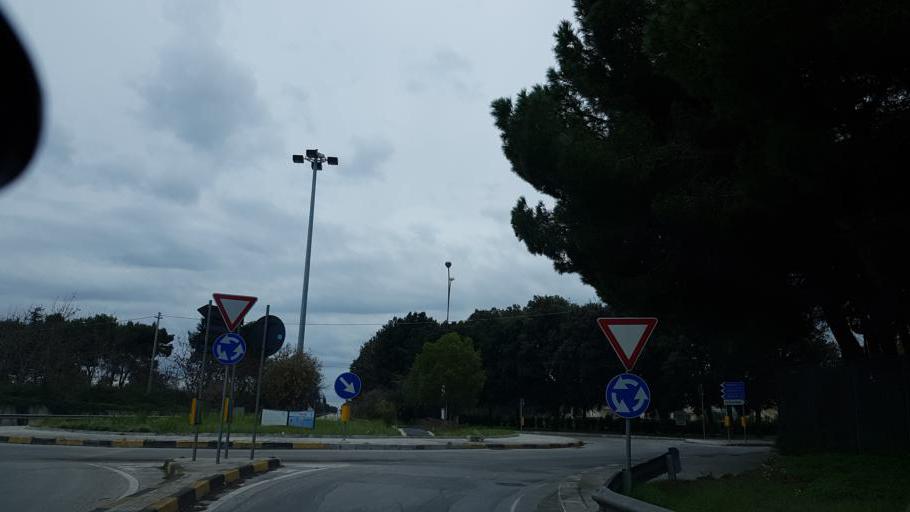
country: IT
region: Apulia
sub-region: Provincia di Brindisi
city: La Rosa
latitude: 40.6099
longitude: 17.9537
